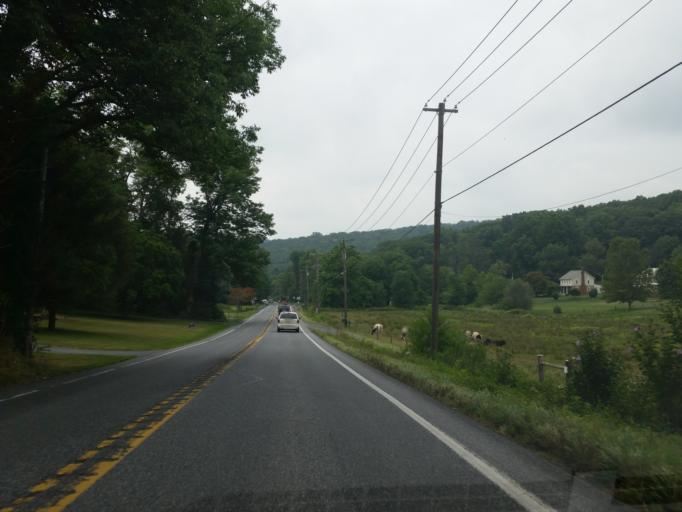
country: US
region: Pennsylvania
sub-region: Lancaster County
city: Brickerville
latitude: 40.2568
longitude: -76.3078
